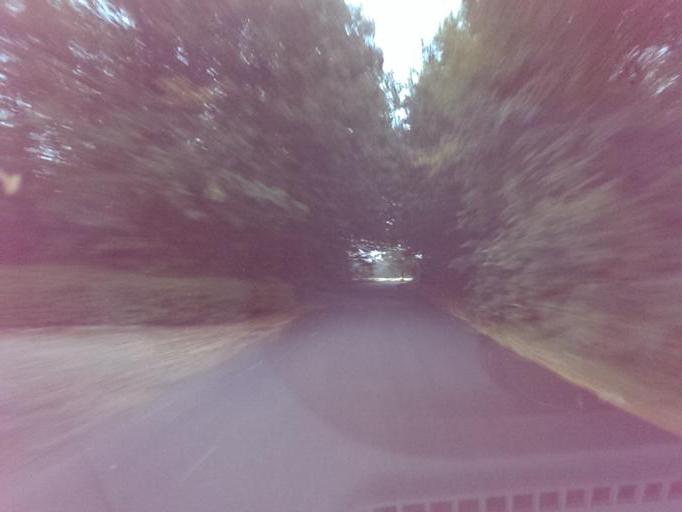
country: DK
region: South Denmark
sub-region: Esbjerg Kommune
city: Bramming
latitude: 55.4722
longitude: 8.7172
